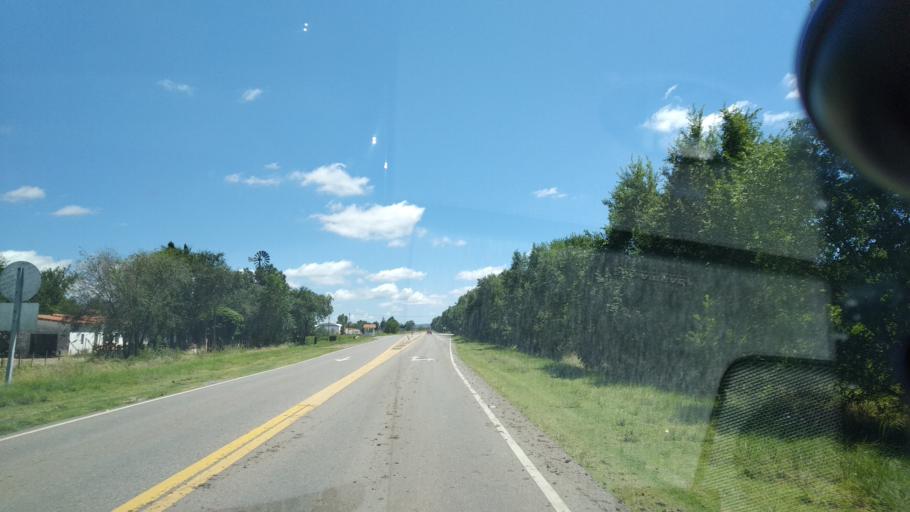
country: AR
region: Cordoba
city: Salsacate
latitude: -31.4995
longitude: -65.1094
